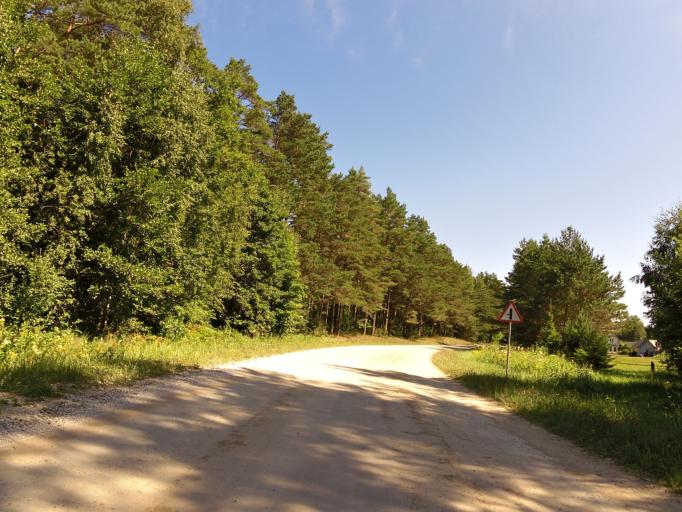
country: EE
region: Hiiumaa
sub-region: Kaerdla linn
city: Kardla
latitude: 58.9301
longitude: 22.3734
